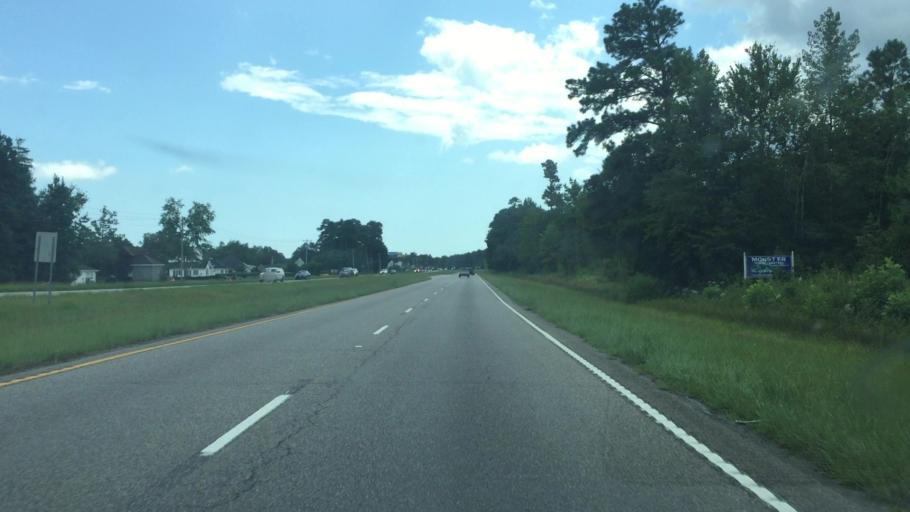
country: US
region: South Carolina
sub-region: Horry County
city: North Myrtle Beach
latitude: 33.9317
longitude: -78.7280
